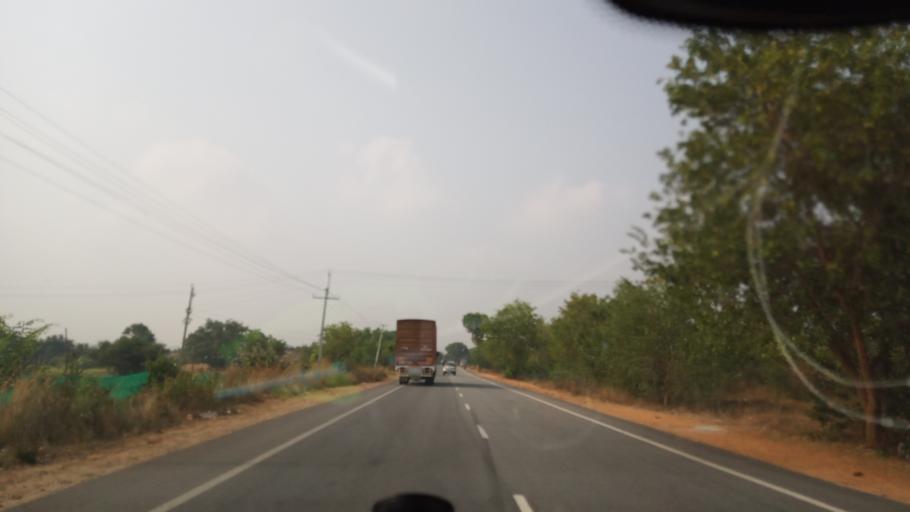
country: IN
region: Karnataka
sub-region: Mandya
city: Nagamangala
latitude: 12.7956
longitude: 76.7511
